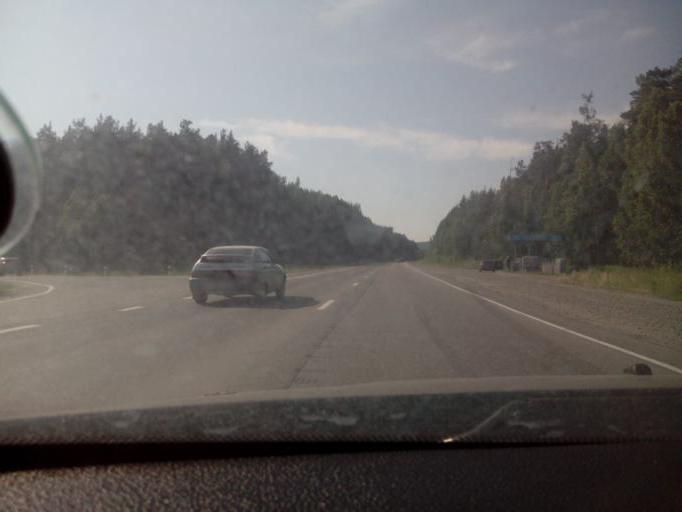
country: RU
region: Sverdlovsk
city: Sredneuralsk
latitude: 57.0672
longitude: 60.4212
